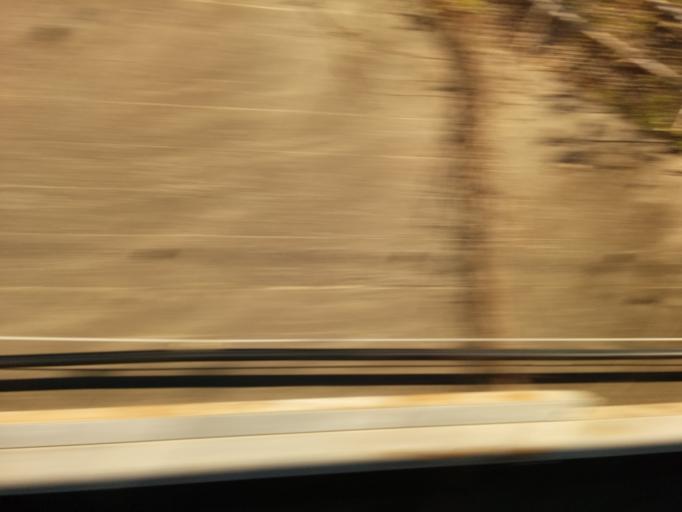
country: JP
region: Shizuoka
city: Kosai-shi
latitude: 34.7011
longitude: 137.5440
